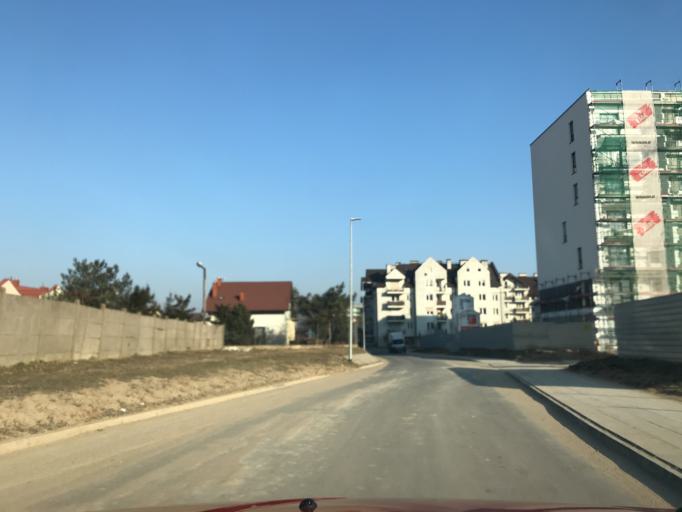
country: PL
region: Greater Poland Voivodeship
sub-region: Kalisz
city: Kalisz
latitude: 51.7620
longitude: 18.0628
